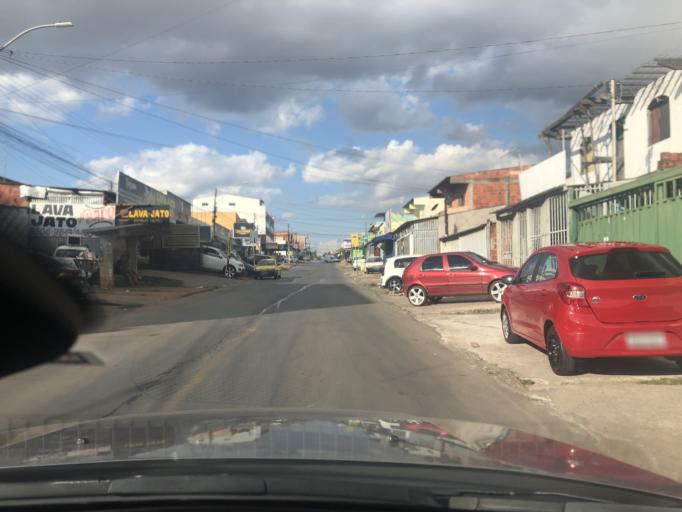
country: BR
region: Federal District
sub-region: Brasilia
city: Brasilia
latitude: -15.9200
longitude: -48.0597
